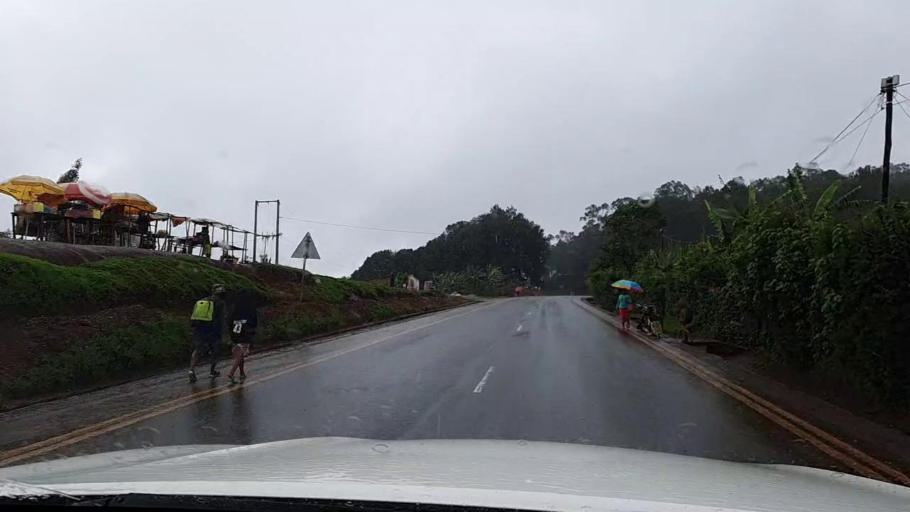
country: RW
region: Western Province
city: Cyangugu
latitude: -2.4626
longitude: 28.9963
